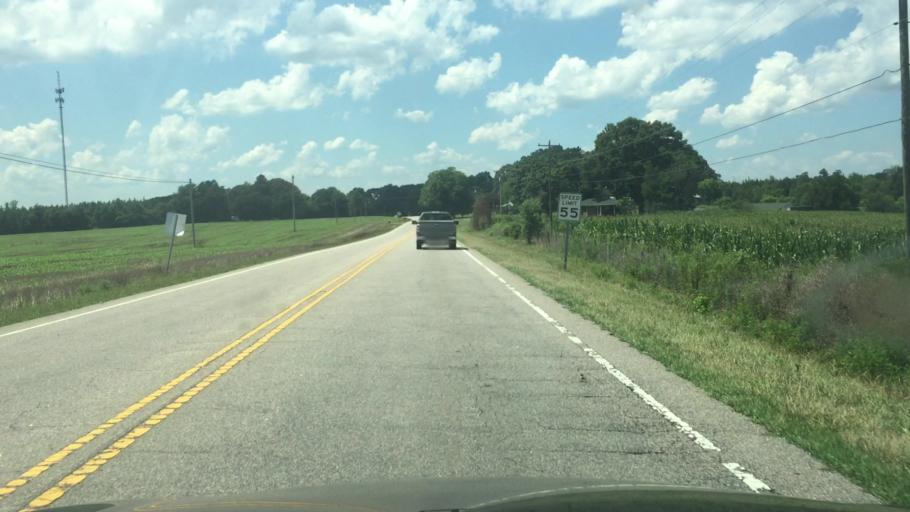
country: US
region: North Carolina
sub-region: Rowan County
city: Enochville
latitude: 35.5740
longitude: -80.6875
